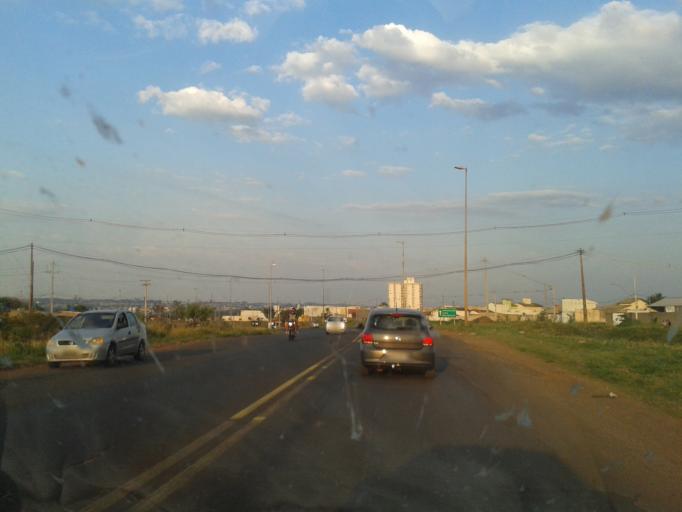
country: BR
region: Minas Gerais
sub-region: Uberlandia
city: Uberlandia
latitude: -18.9089
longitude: -48.3340
